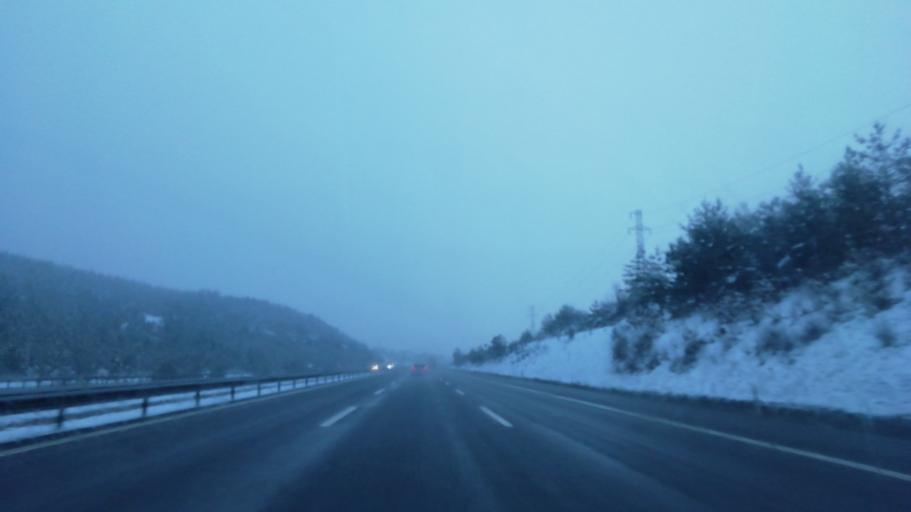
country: TR
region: Bolu
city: Bolu
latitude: 40.7554
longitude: 31.5733
